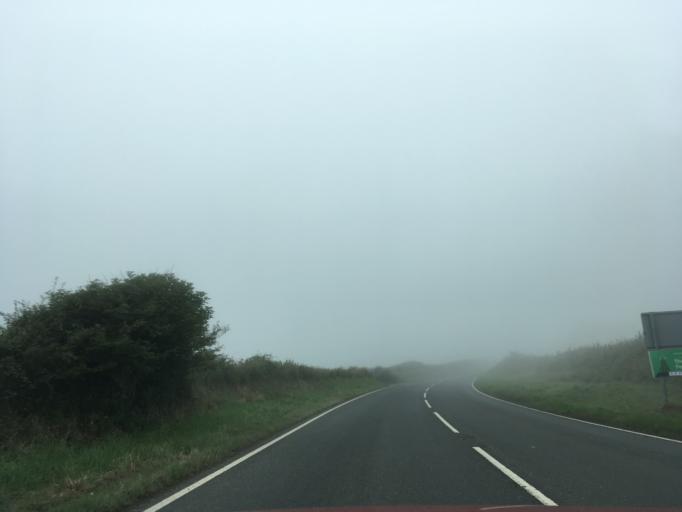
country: GB
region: Wales
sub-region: Pembrokeshire
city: Llanrhian
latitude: 51.8676
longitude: -5.1291
